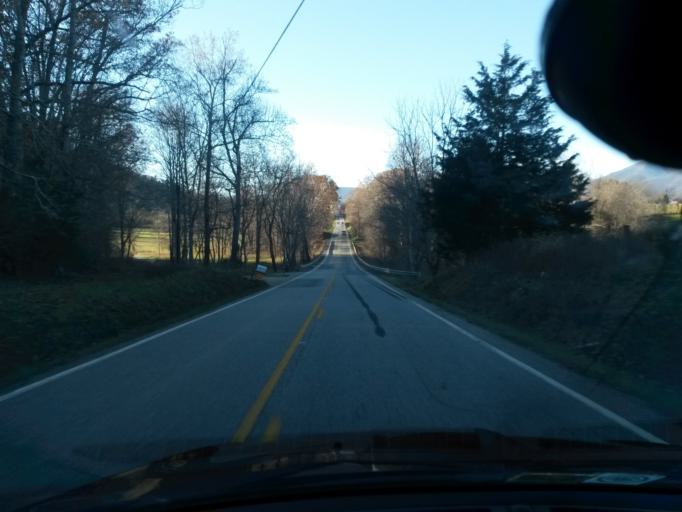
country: US
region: Virginia
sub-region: Amherst County
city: Amherst
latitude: 37.6453
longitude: -79.1261
